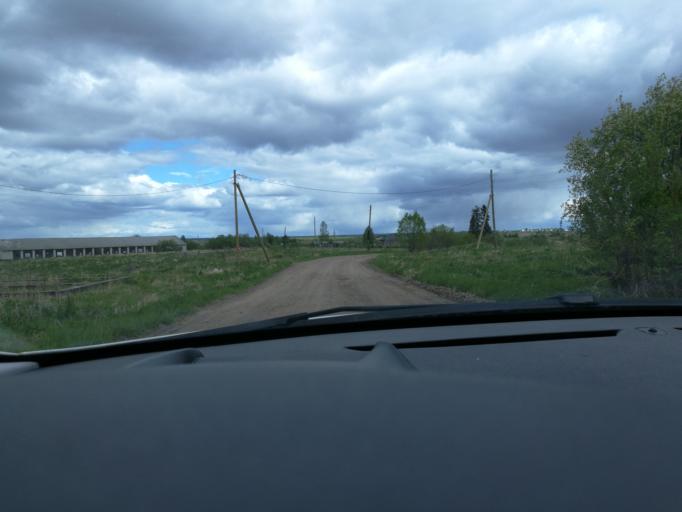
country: RU
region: Arkhangelskaya
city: Lukovetskiy
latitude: 64.2535
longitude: 41.7927
